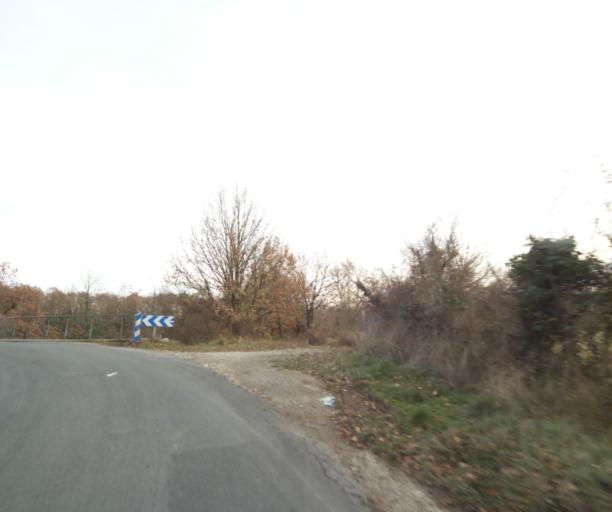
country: FR
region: Poitou-Charentes
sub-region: Departement de la Charente-Maritime
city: Fontcouverte
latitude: 45.8001
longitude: -0.5761
